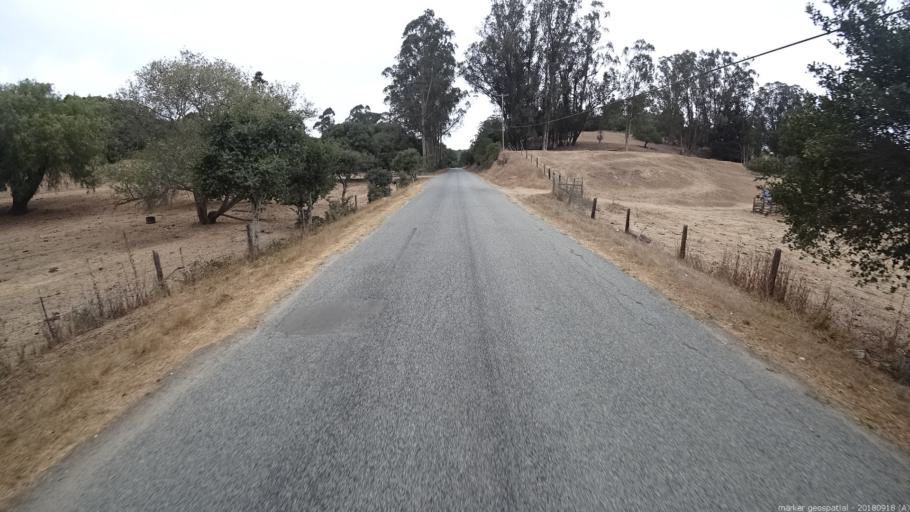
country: US
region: California
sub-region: Monterey County
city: Prunedale
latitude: 36.7807
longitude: -121.6418
